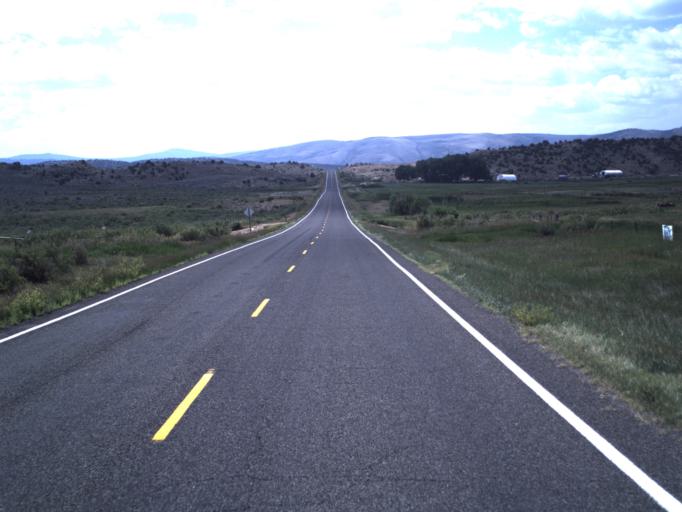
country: US
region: Utah
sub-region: Daggett County
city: Manila
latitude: 40.9653
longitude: -109.7131
